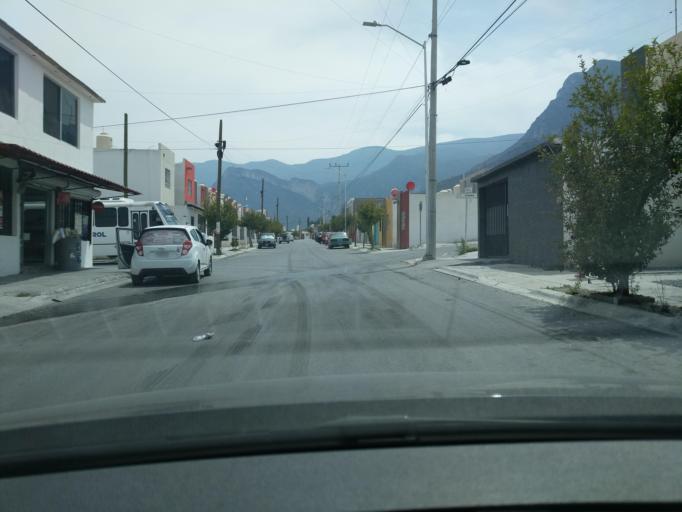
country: MX
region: Coahuila
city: Saltillo
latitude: 25.3458
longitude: -101.0079
